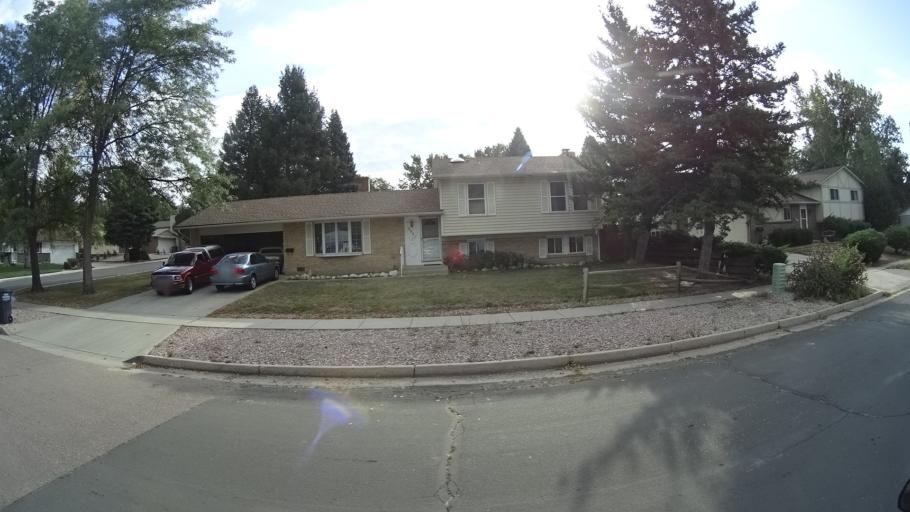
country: US
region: Colorado
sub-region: El Paso County
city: Cimarron Hills
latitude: 38.8653
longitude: -104.7539
